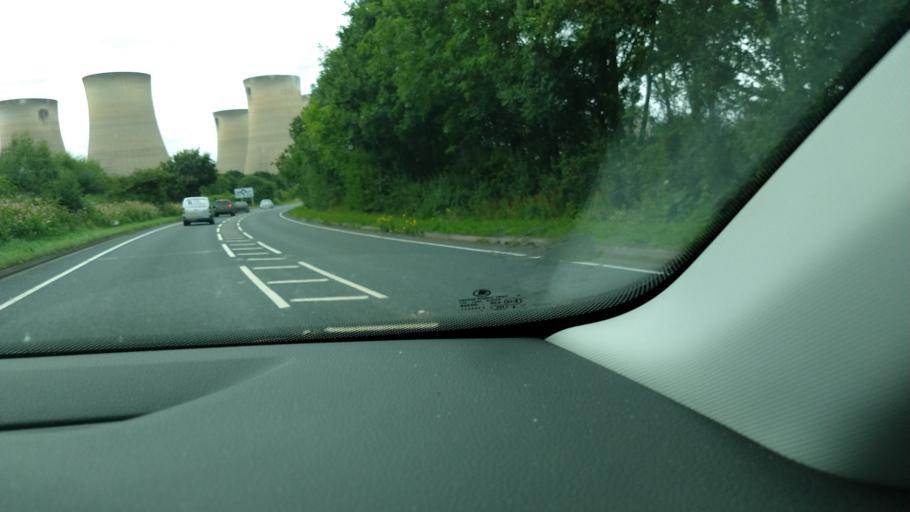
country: GB
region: England
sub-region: North Yorkshire
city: Camblesforth
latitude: 53.7265
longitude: -0.9907
